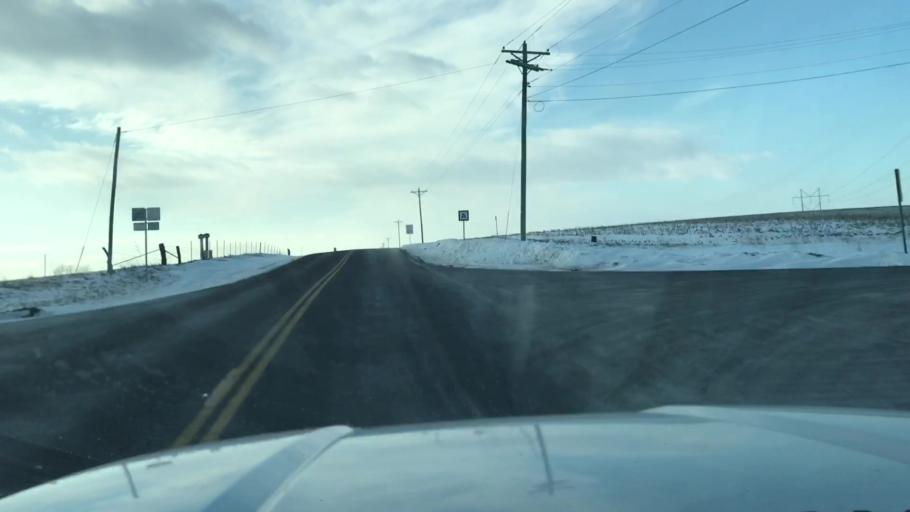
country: US
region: Missouri
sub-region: Nodaway County
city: Maryville
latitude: 40.2019
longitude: -94.9535
